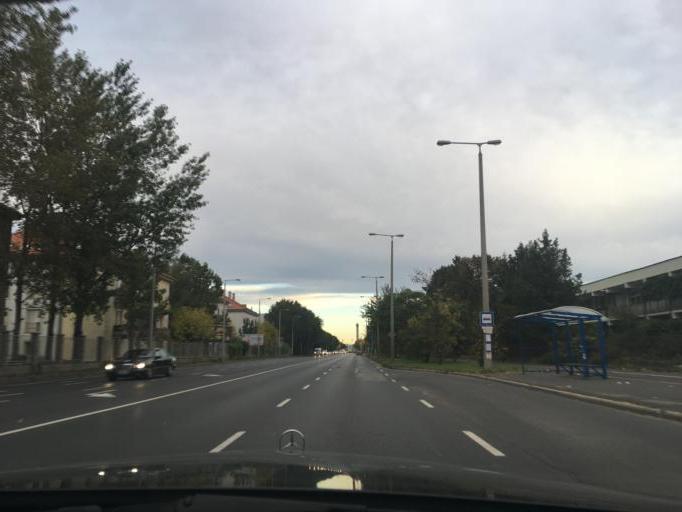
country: HU
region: Hajdu-Bihar
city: Debrecen
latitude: 47.5040
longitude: 21.6308
